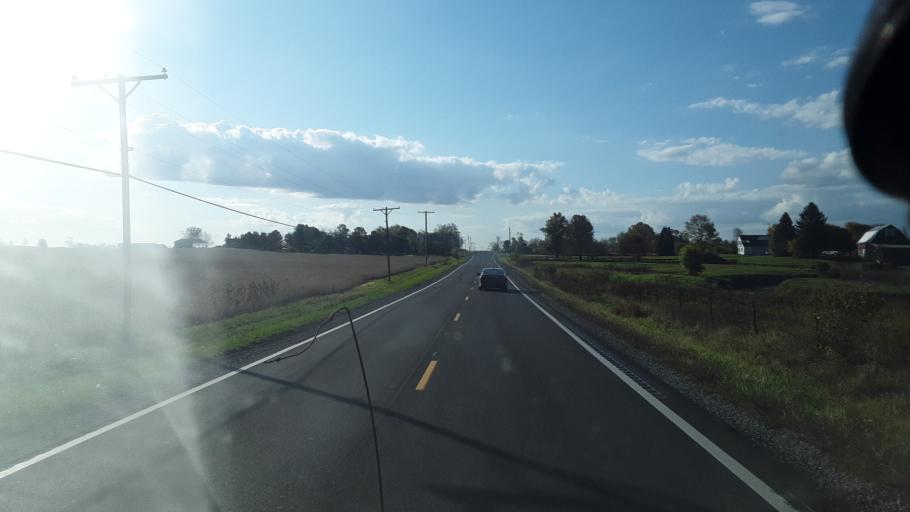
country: US
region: Ohio
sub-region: Fayette County
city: Jeffersonville
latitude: 39.6378
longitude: -83.5334
